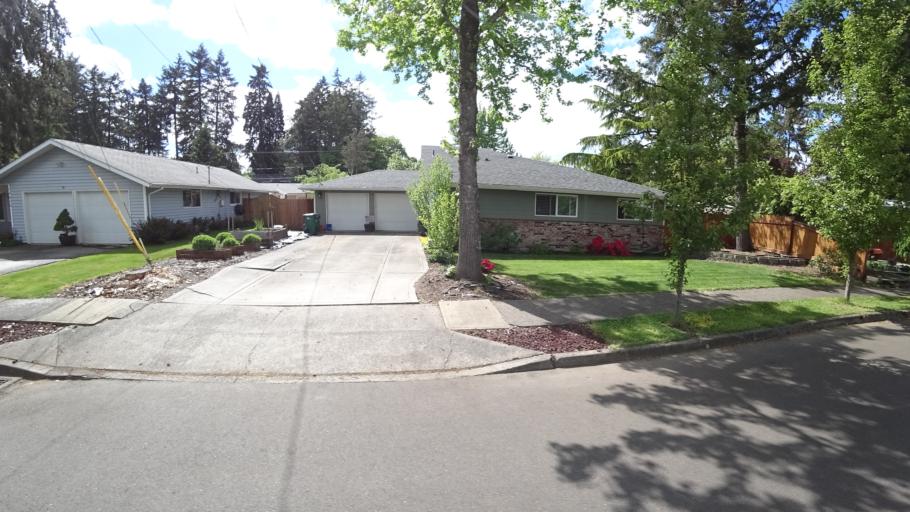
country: US
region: Oregon
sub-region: Washington County
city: Beaverton
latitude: 45.4791
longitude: -122.8206
